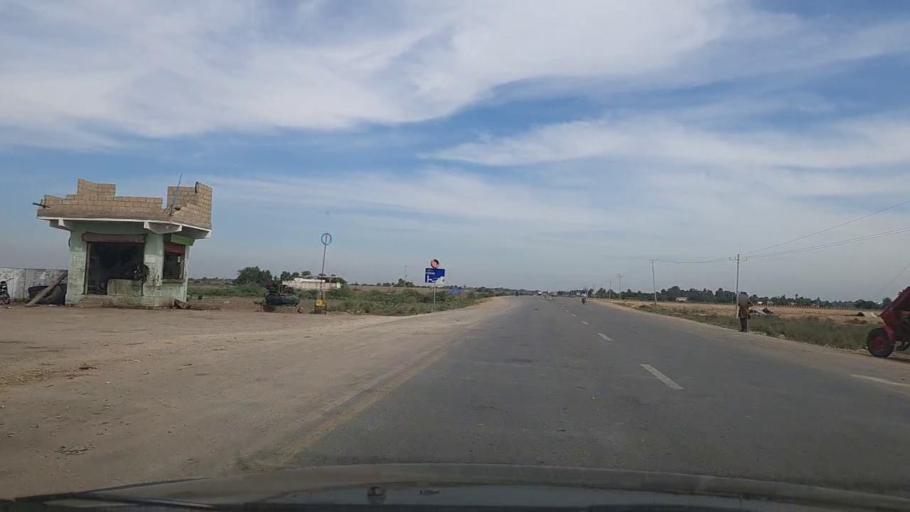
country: PK
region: Sindh
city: Thatta
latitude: 24.7692
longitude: 67.9392
